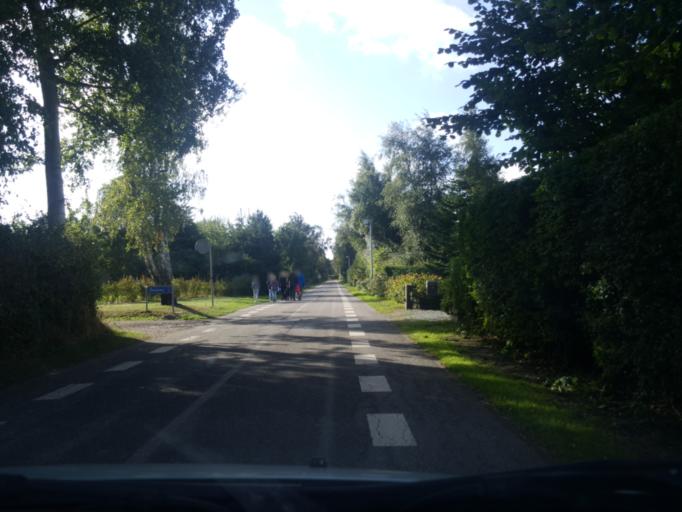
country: DK
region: Zealand
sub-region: Guldborgsund Kommune
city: Nykobing Falster
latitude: 54.6545
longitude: 11.9567
